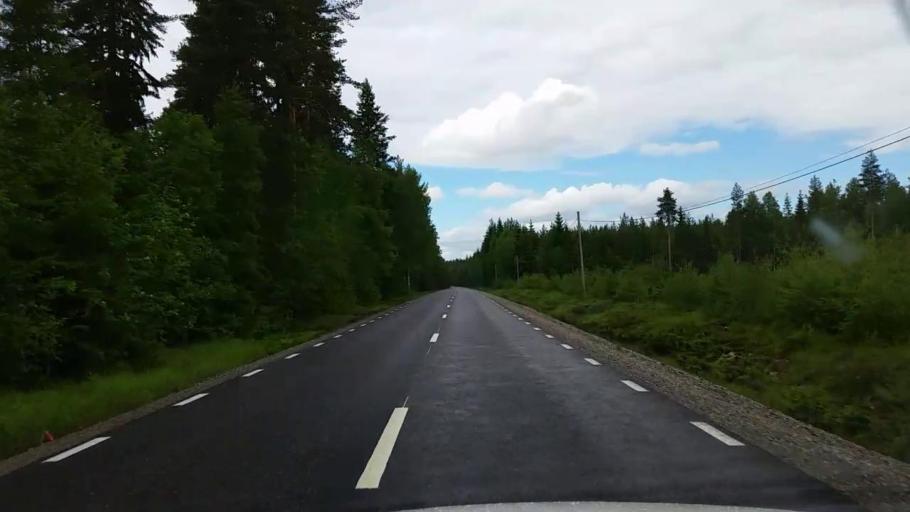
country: SE
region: Gaevleborg
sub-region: Sandvikens Kommun
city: Jarbo
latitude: 60.8542
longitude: 16.4426
